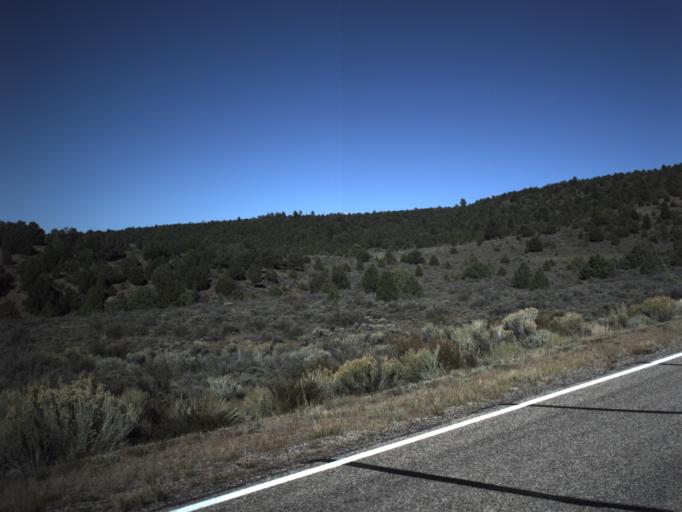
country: US
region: Utah
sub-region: Garfield County
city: Panguitch
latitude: 37.7675
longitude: -112.5371
